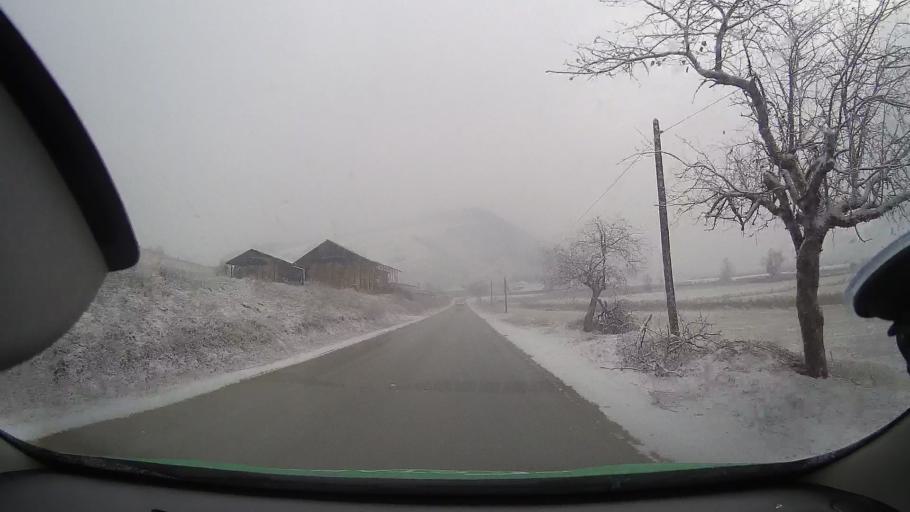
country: RO
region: Alba
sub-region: Comuna Lopadea Noua
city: Lopadea Noua
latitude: 46.2995
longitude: 23.8093
